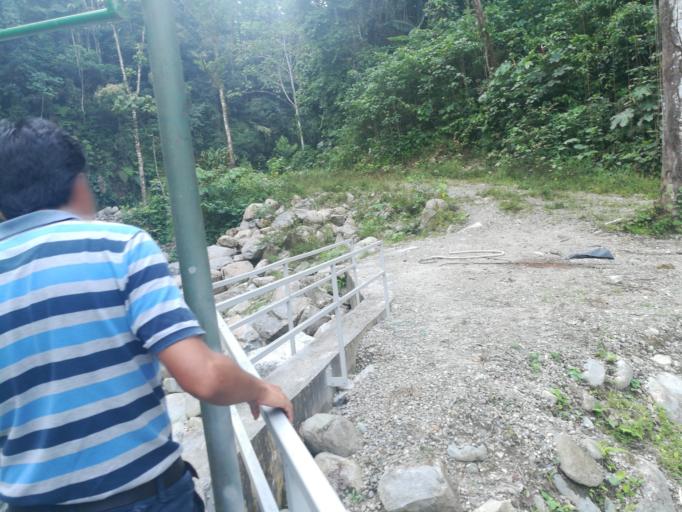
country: EC
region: Napo
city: Archidona
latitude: -0.9460
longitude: -77.8942
